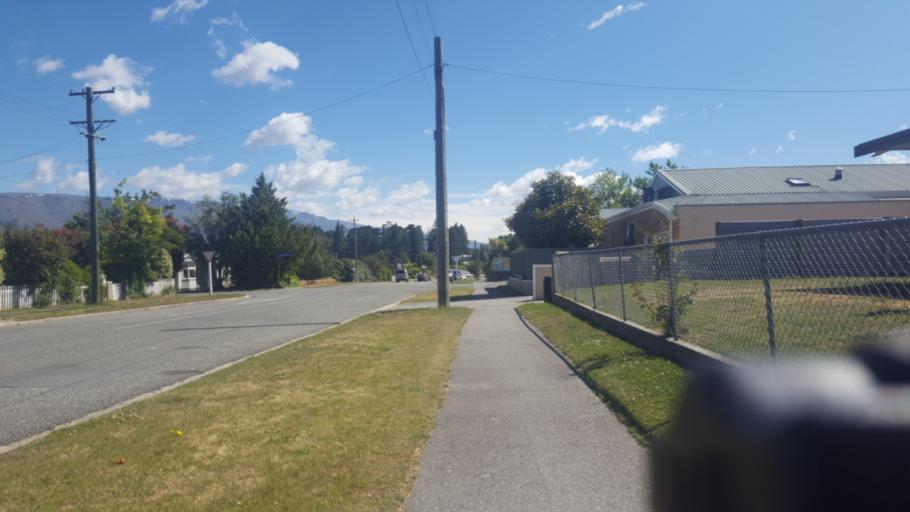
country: NZ
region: Otago
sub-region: Queenstown-Lakes District
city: Wanaka
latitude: -45.0467
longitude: 169.2084
